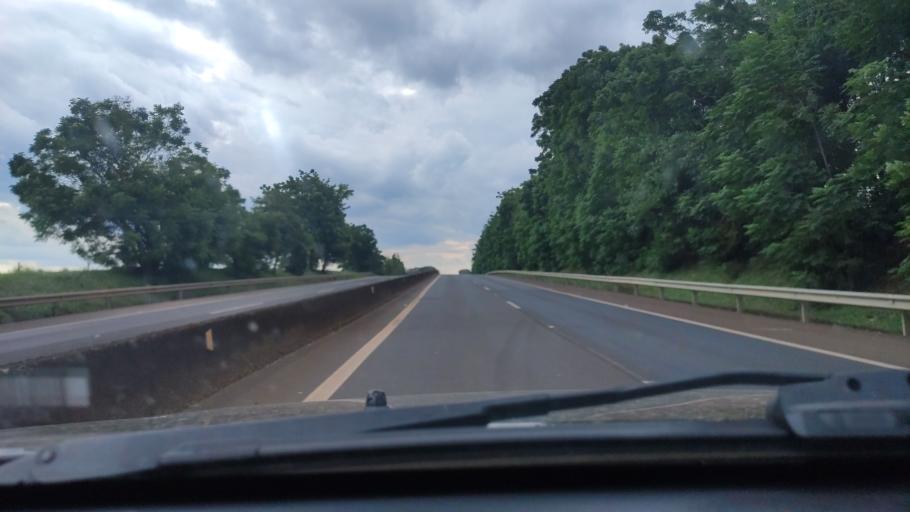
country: BR
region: Sao Paulo
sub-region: Ourinhos
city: Ourinhos
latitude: -22.8438
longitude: -50.0116
